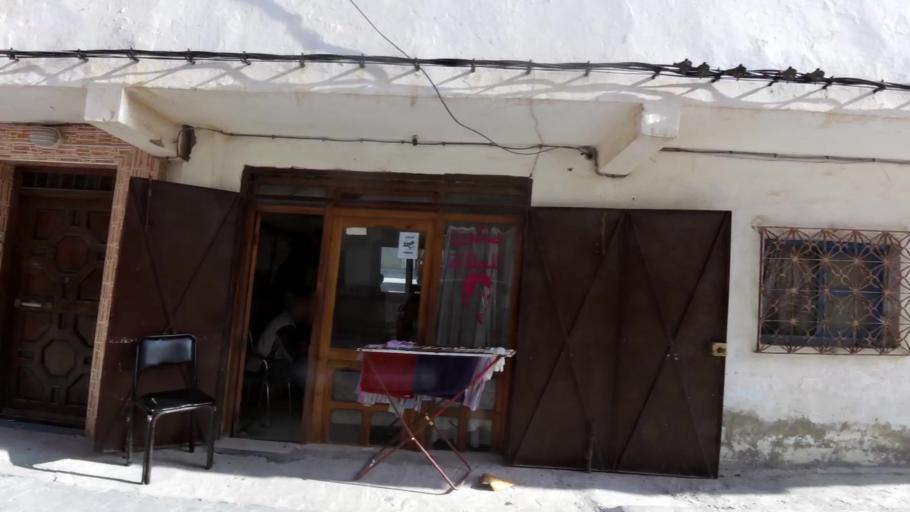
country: MA
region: Tanger-Tetouan
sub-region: Tetouan
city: Martil
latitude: 35.6103
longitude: -5.2728
